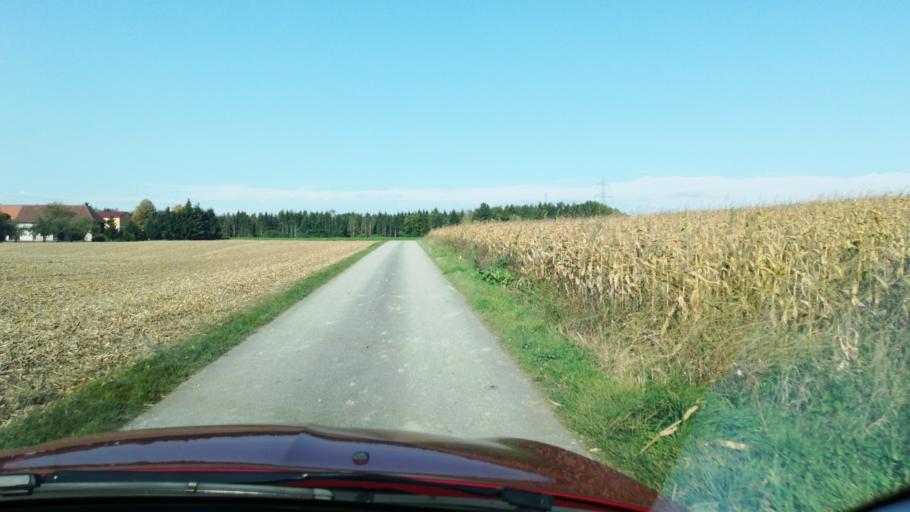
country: AT
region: Upper Austria
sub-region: Politischer Bezirk Kirchdorf an der Krems
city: Kremsmunster
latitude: 48.0974
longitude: 14.1609
